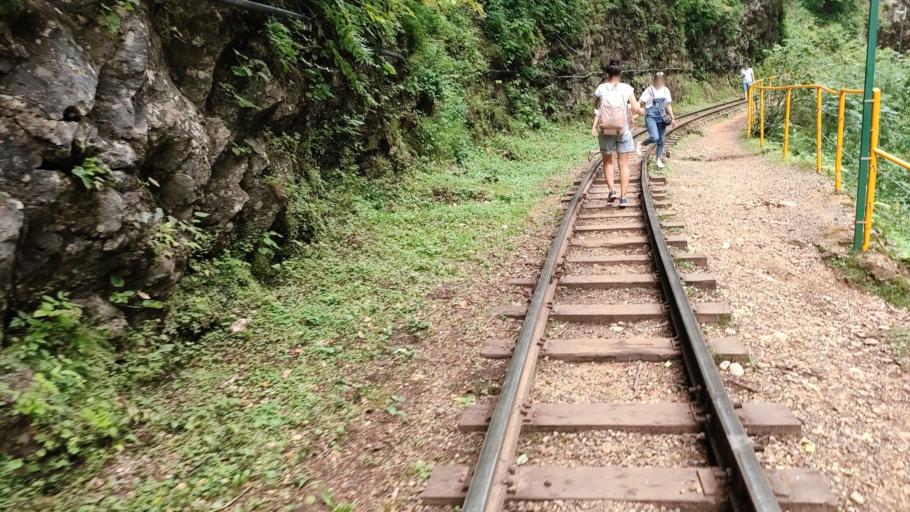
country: RU
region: Krasnodarskiy
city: Neftegorsk
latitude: 44.2183
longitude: 39.9088
